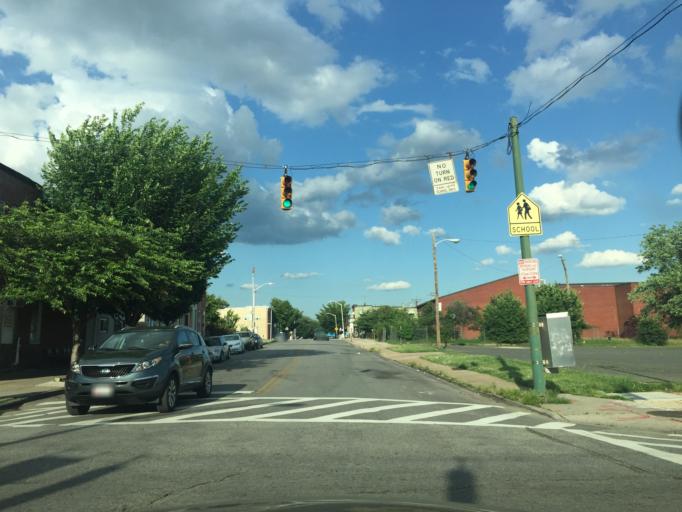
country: US
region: Maryland
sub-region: City of Baltimore
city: Baltimore
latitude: 39.3036
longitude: -76.5855
